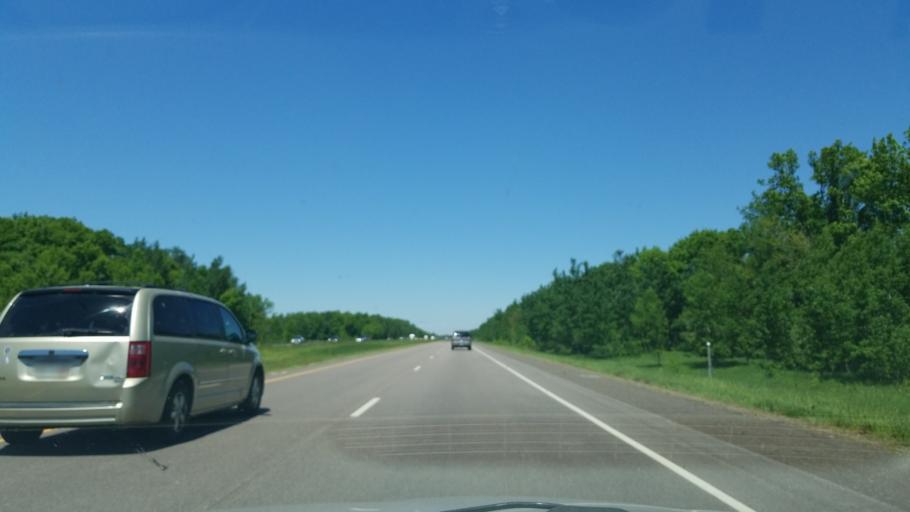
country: US
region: Minnesota
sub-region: Chisago County
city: Rush City
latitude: 45.6571
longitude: -92.9921
